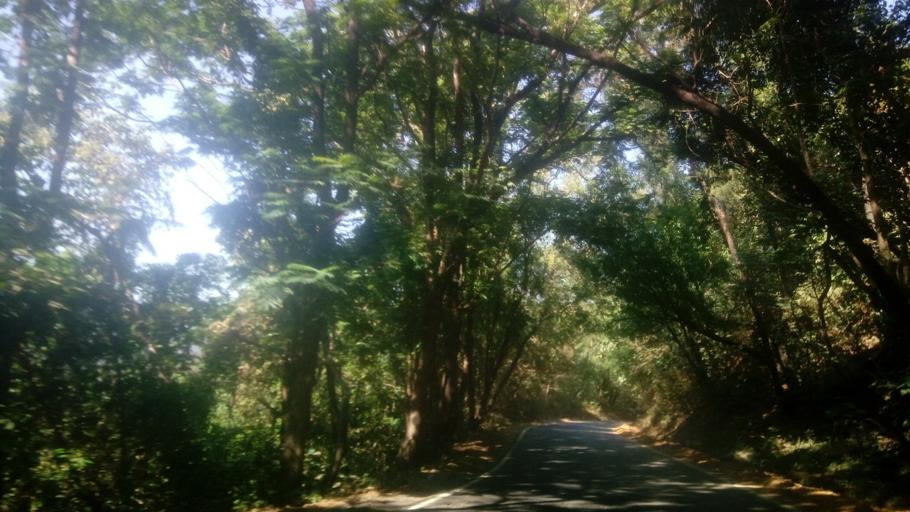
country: IN
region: Goa
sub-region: North Goa
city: Valpoy
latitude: 15.6143
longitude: 74.1194
